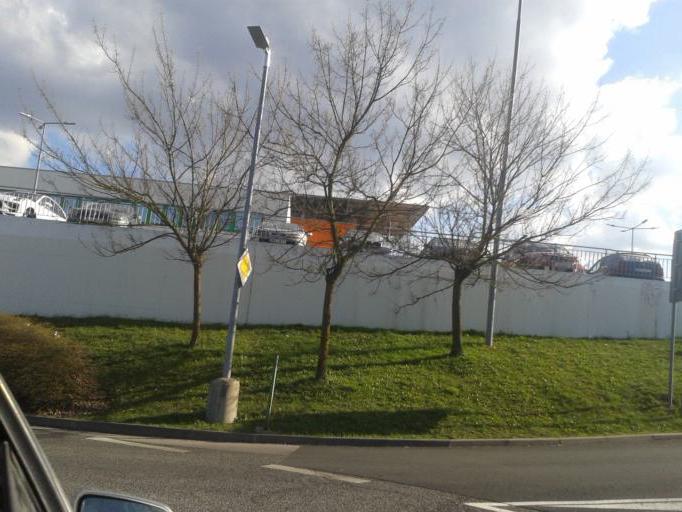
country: CZ
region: Central Bohemia
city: Hostivice
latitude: 50.0536
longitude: 14.2956
